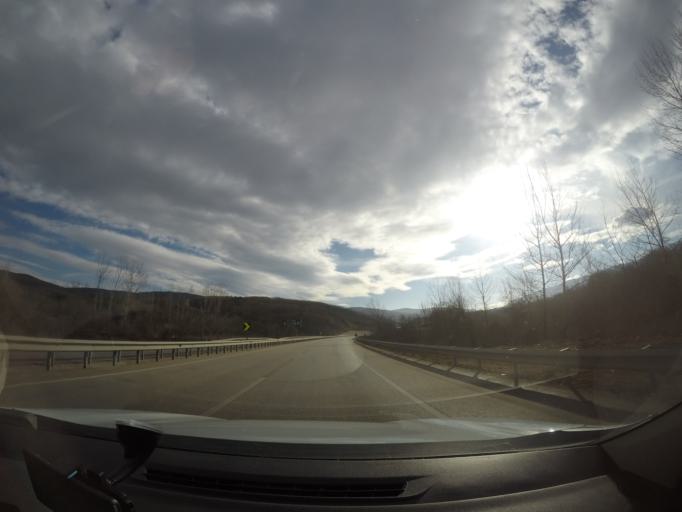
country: TR
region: Bursa
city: Tahtakopru
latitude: 39.9557
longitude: 29.6767
